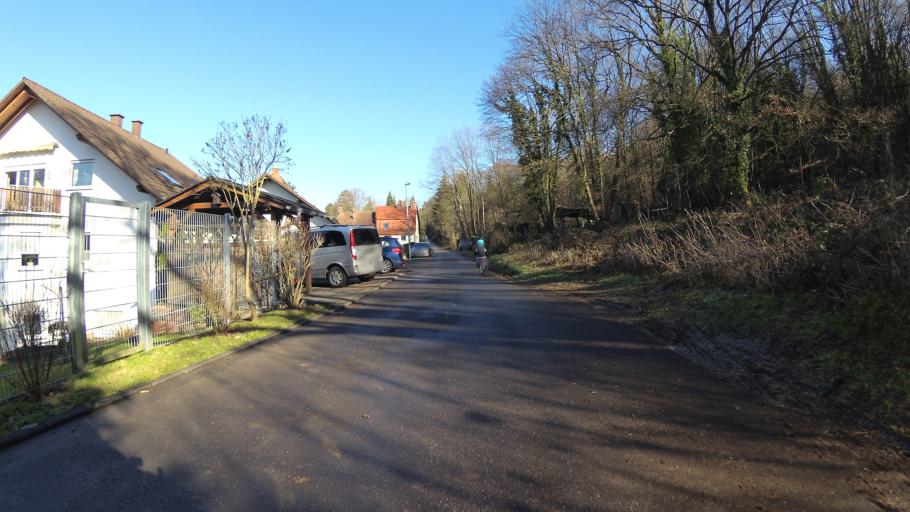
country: DE
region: Saarland
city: Sulzbach
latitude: 49.2975
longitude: 7.0673
